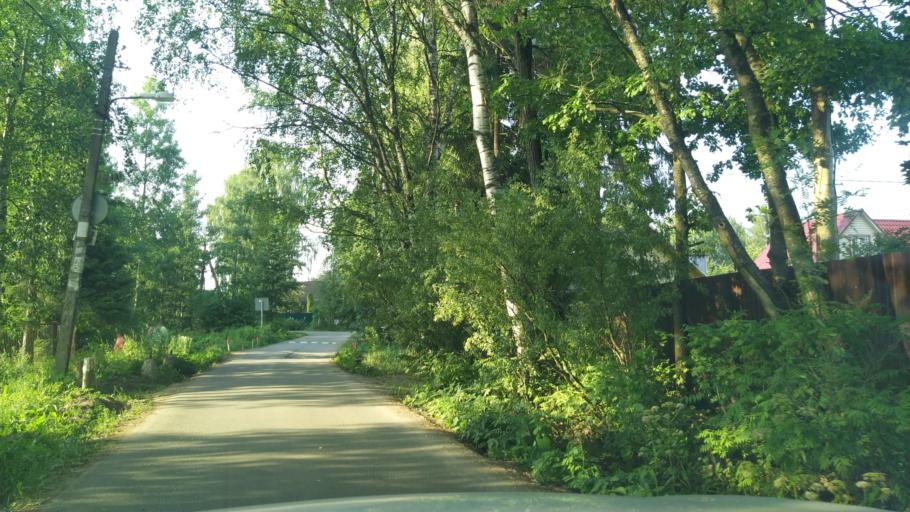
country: RU
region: Leningrad
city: Koltushi
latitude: 59.8945
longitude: 30.7329
